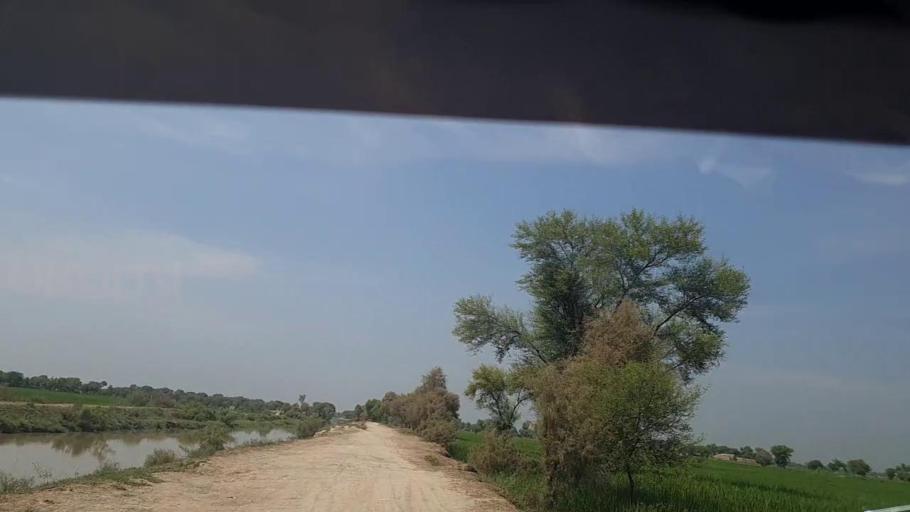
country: PK
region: Sindh
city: Thul
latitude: 28.1956
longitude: 68.7070
